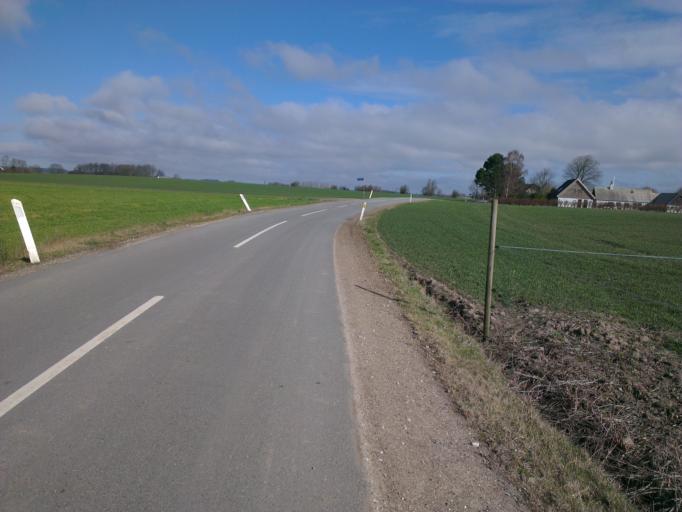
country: DK
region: Capital Region
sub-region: Hillerod Kommune
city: Skaevinge
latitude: 55.8694
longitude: 12.1150
